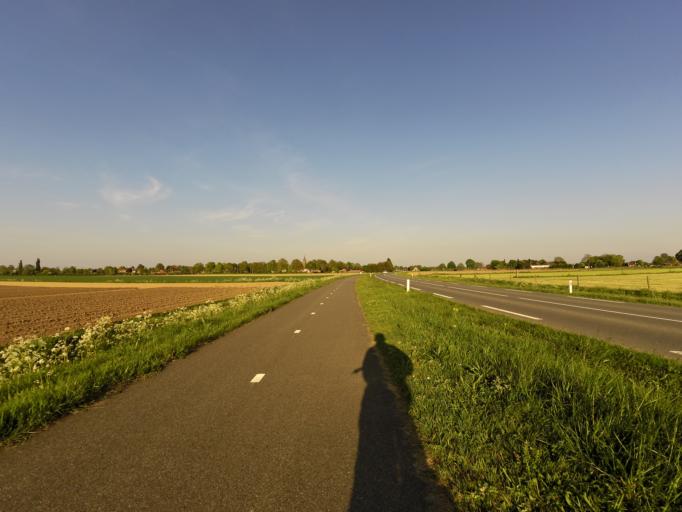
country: NL
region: Gelderland
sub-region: Oude IJsselstreek
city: Gendringen
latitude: 51.8871
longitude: 6.3494
